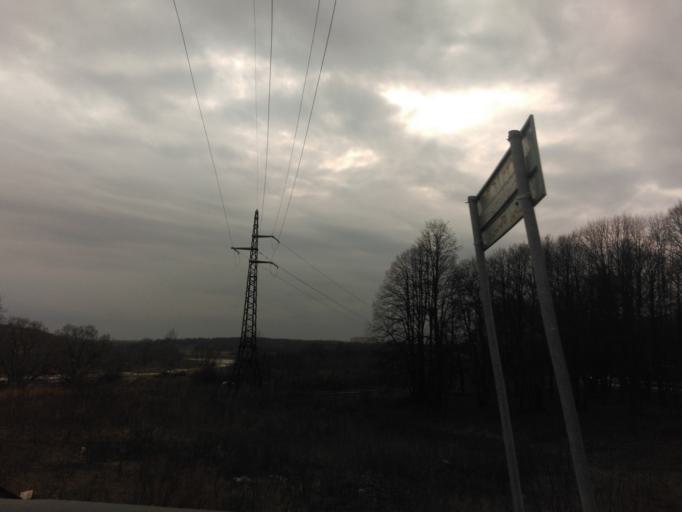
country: RU
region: Moskovskaya
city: Nikolina Gora
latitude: 55.7237
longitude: 37.0669
